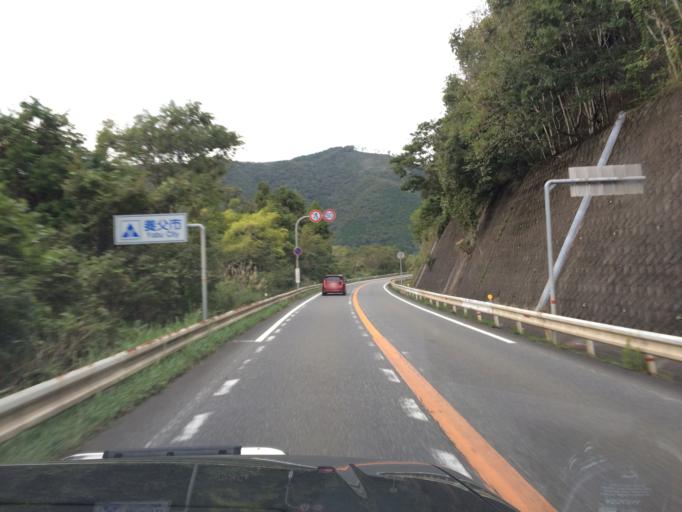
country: JP
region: Hyogo
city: Toyooka
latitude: 35.3696
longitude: 134.8190
